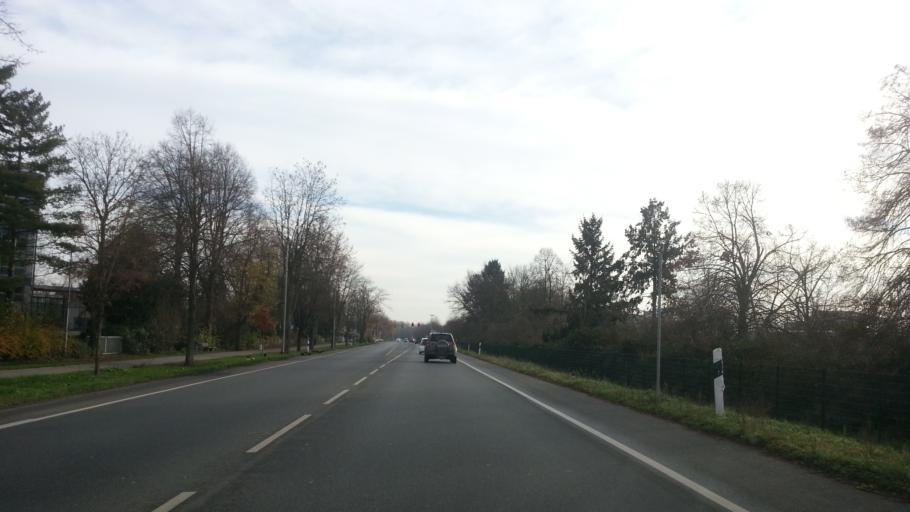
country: DE
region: Hesse
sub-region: Regierungsbezirk Darmstadt
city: Gross-Gerau
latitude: 49.9166
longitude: 8.4768
